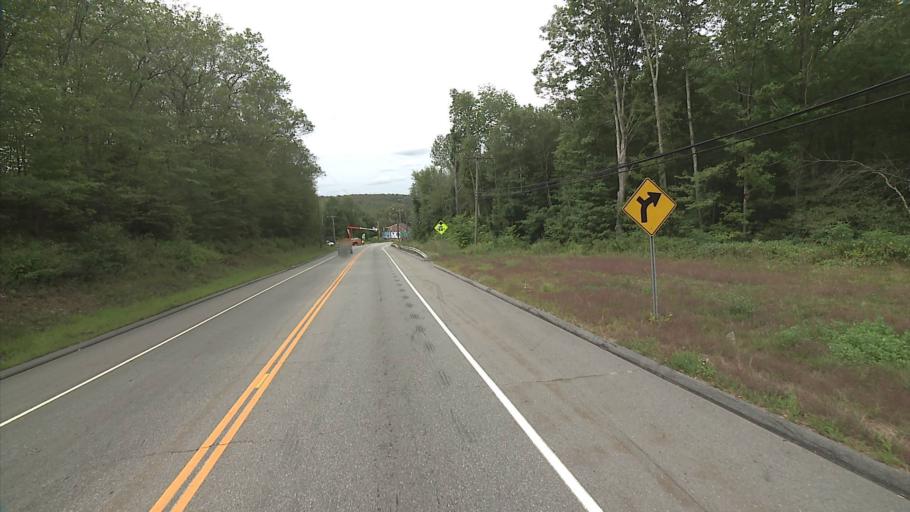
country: US
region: Connecticut
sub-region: New London County
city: Montville Center
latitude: 41.4270
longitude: -72.2132
